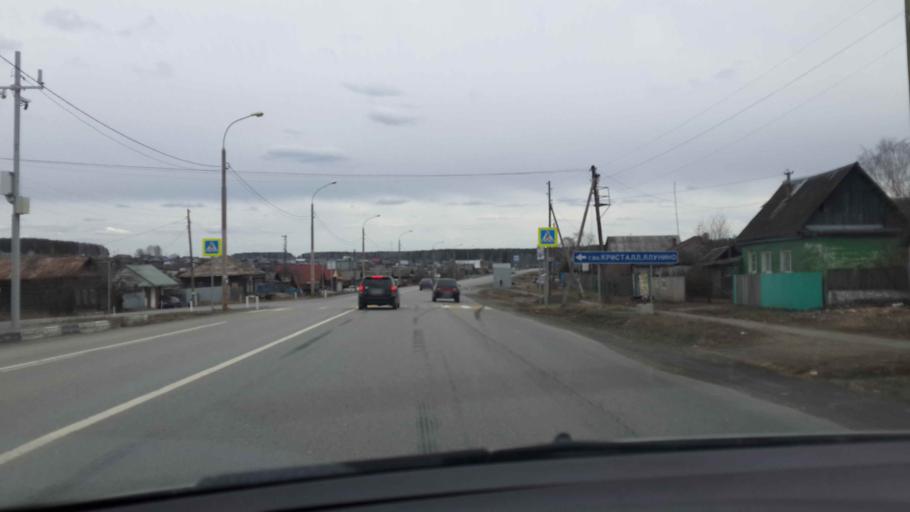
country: RU
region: Sverdlovsk
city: Beloyarskiy
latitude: 56.7713
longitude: 61.4471
